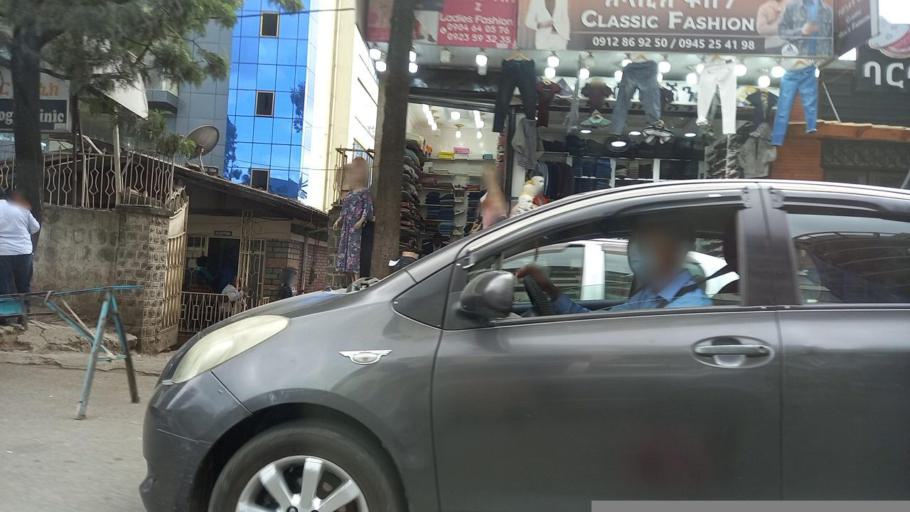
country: ET
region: Adis Abeba
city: Addis Ababa
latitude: 9.0207
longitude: 38.7980
